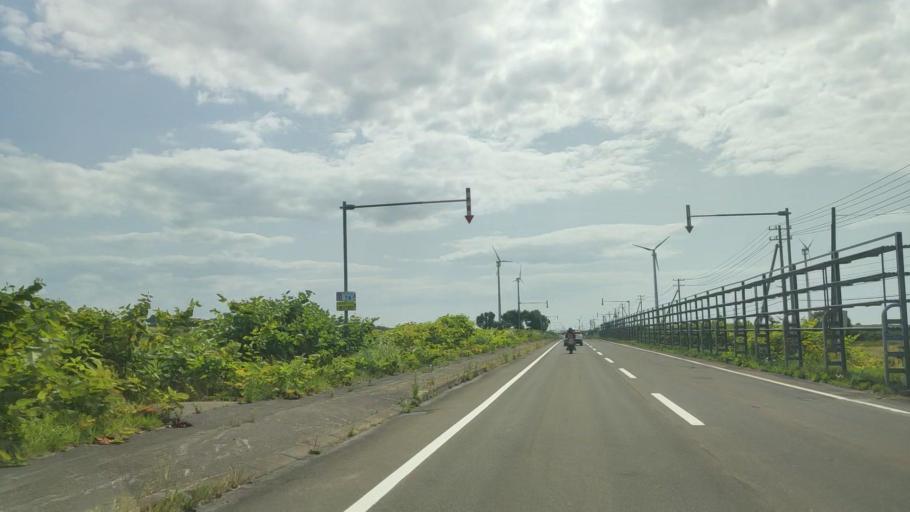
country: JP
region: Hokkaido
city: Rumoi
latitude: 44.3926
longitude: 141.7173
